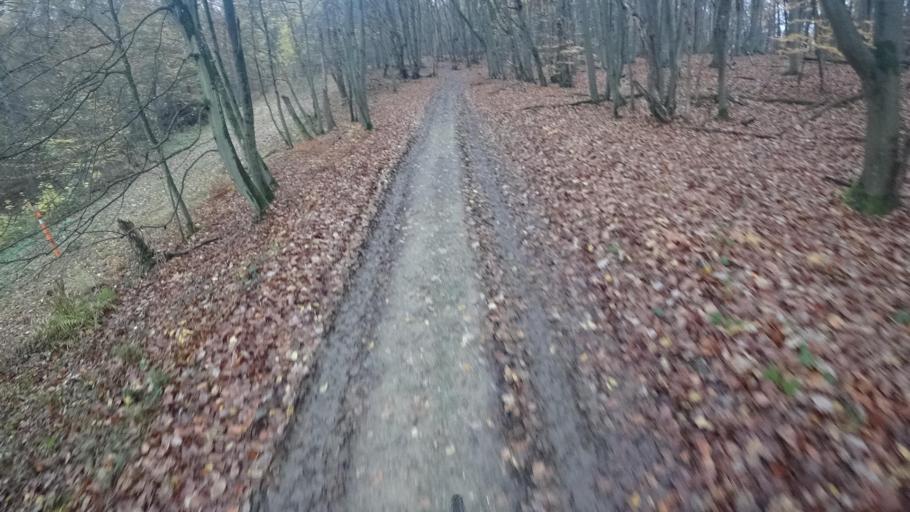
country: DE
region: Rheinland-Pfalz
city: Rech
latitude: 50.5159
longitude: 7.0463
